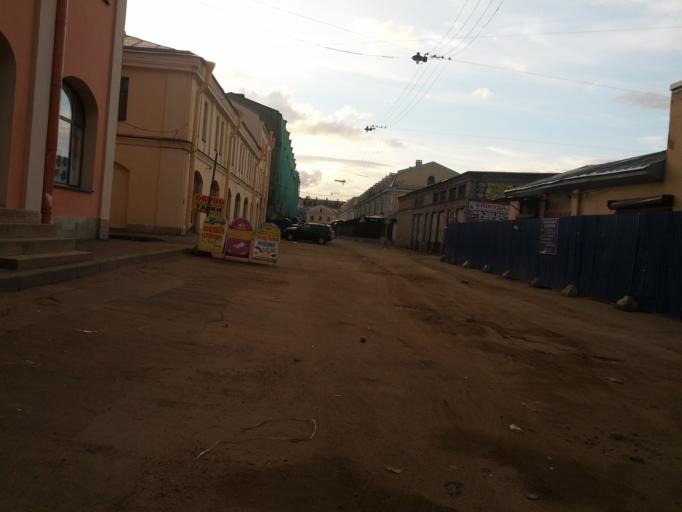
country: RU
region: St.-Petersburg
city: Saint Petersburg
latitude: 59.9283
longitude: 30.3309
